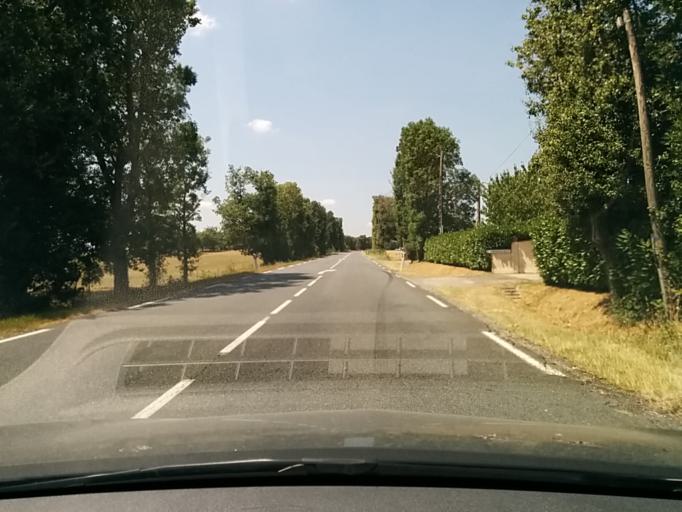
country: FR
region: Midi-Pyrenees
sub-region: Departement du Gers
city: Gimont
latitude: 43.6033
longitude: 1.0027
